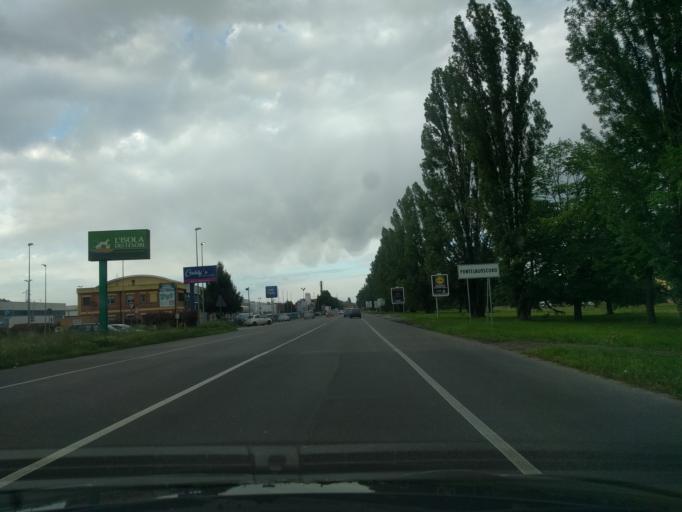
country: IT
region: Veneto
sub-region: Provincia di Rovigo
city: Santa Maria Maddalena
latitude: 44.8732
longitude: 11.6022
